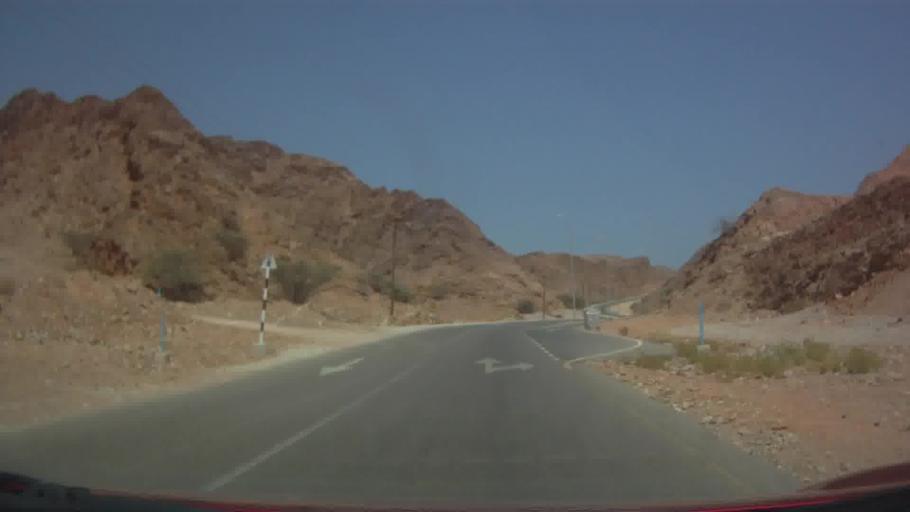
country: OM
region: Muhafazat Masqat
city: Muscat
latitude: 23.5110
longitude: 58.6771
